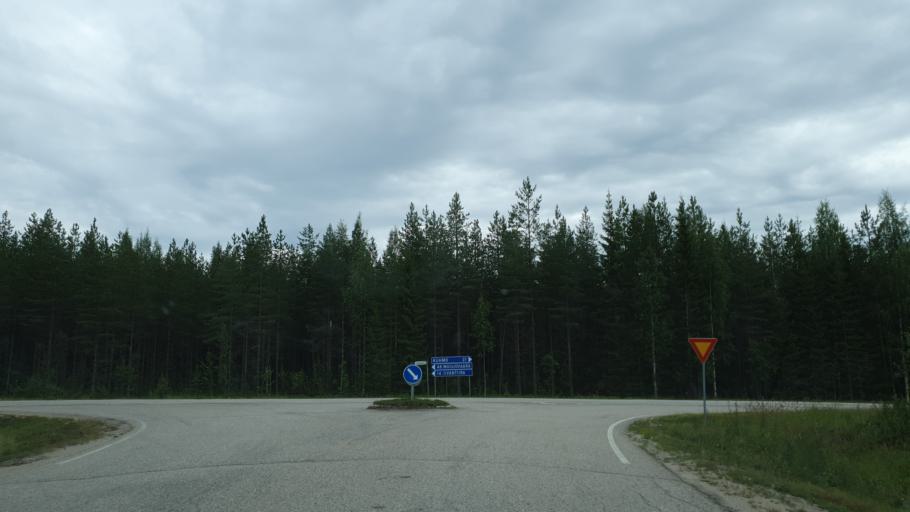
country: FI
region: Kainuu
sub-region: Kehys-Kainuu
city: Kuhmo
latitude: 64.3155
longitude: 29.4511
